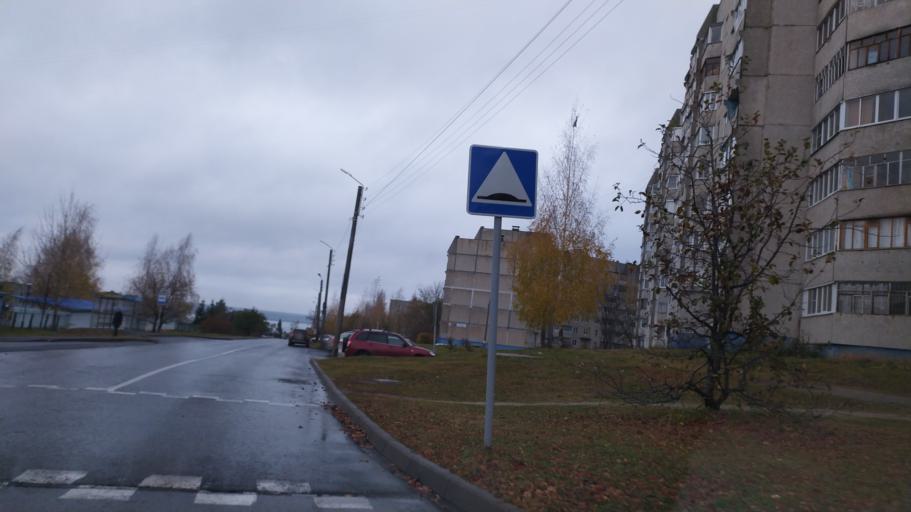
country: RU
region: Chuvashia
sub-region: Cheboksarskiy Rayon
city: Cheboksary
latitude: 56.1437
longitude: 47.1614
